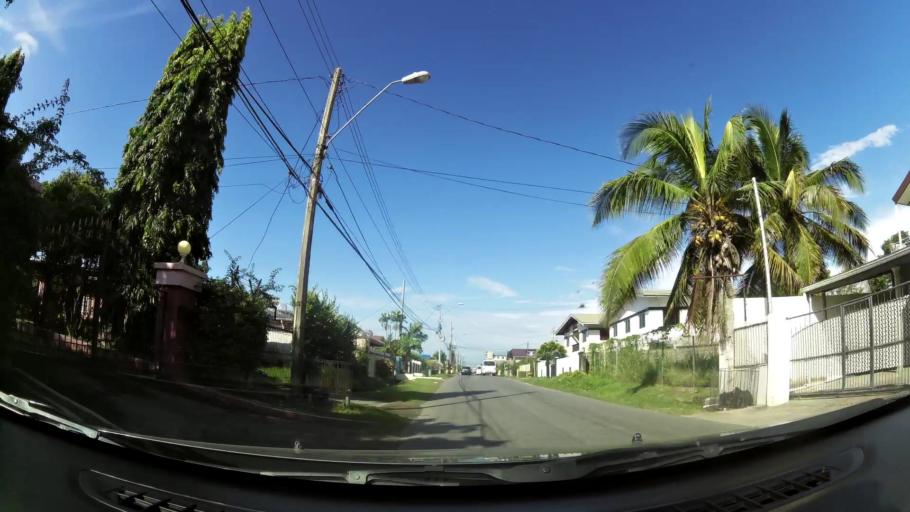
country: TT
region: Chaguanas
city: Chaguanas
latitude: 10.5257
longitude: -61.3992
